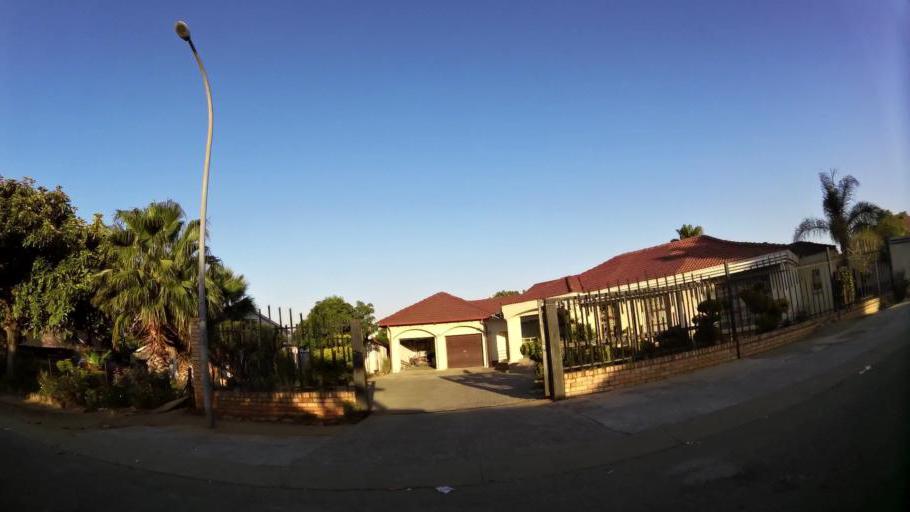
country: ZA
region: North-West
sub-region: Bojanala Platinum District Municipality
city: Rustenburg
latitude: -25.6383
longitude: 27.2034
